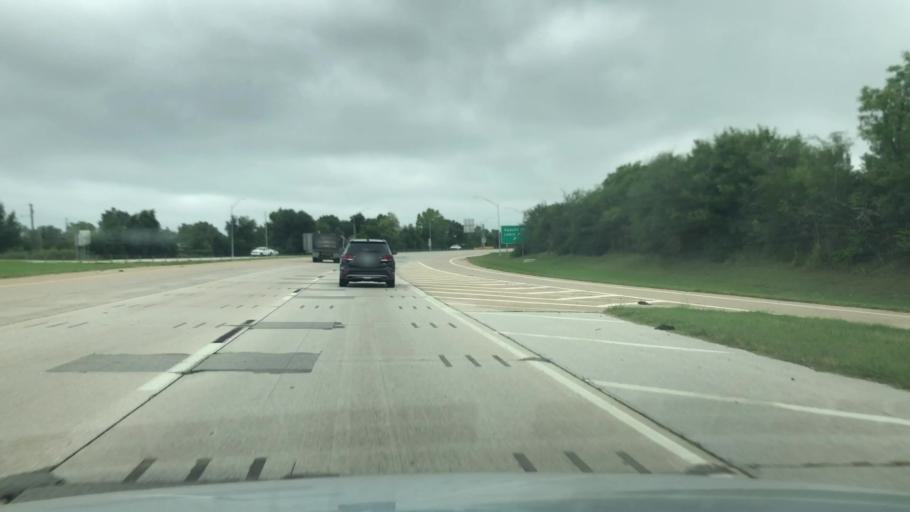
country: US
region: Oklahoma
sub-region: Tulsa County
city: Turley
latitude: 36.1960
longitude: -95.9523
